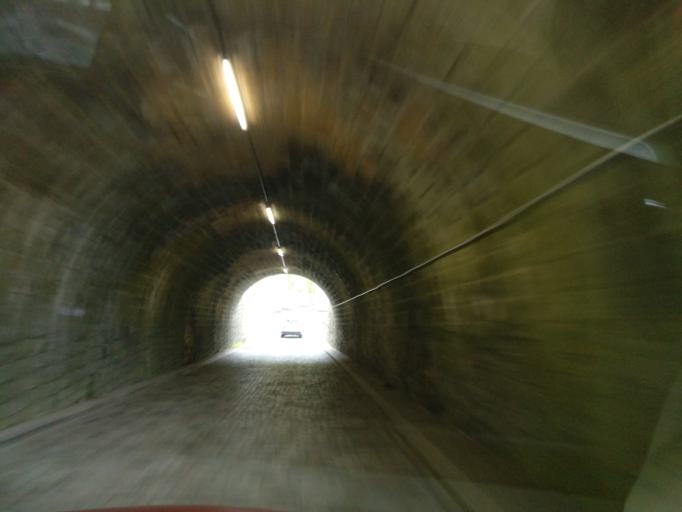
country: LU
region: Luxembourg
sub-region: Canton de Luxembourg
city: Luxembourg
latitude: 49.6208
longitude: 6.1337
